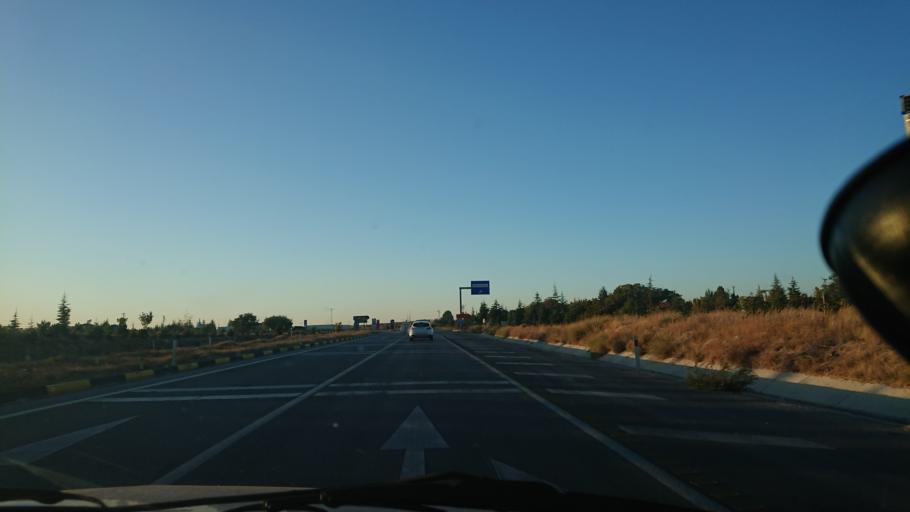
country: TR
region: Eskisehir
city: Mahmudiye
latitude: 39.4746
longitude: 30.9926
